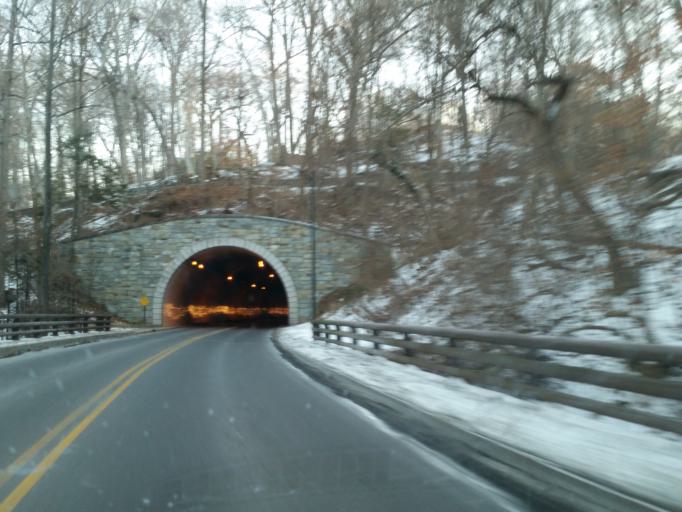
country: US
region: Washington, D.C.
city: Washington, D.C.
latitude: 38.9239
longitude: -77.0486
